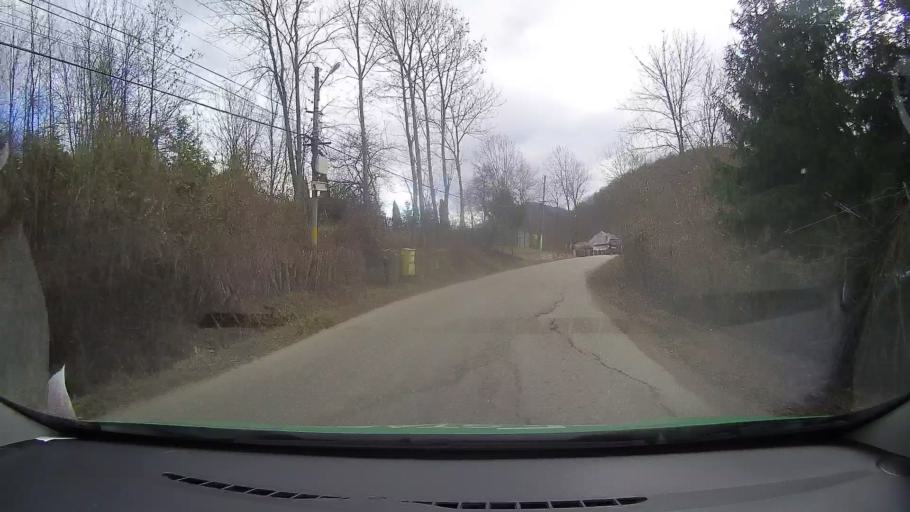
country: RO
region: Dambovita
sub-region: Comuna Visinesti
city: Visinesti
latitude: 45.0986
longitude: 25.5757
